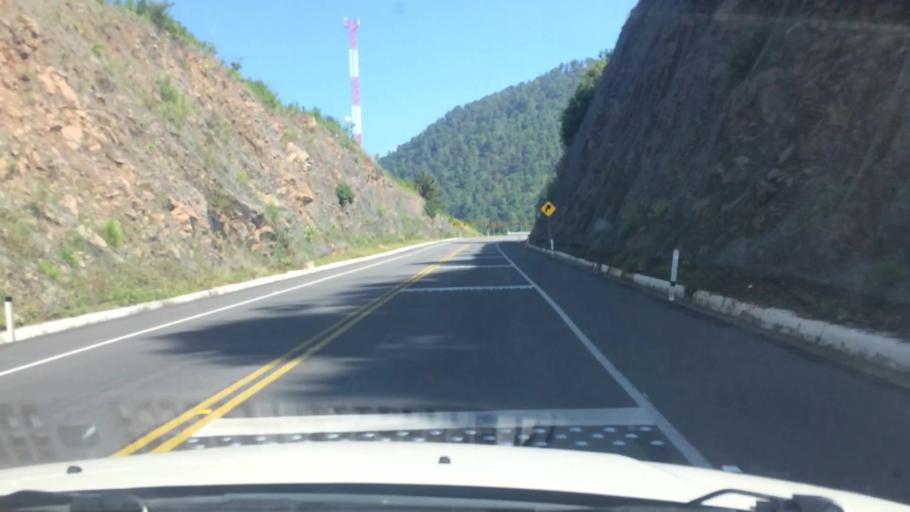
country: MX
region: Mexico
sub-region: Amanalco
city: Polvillos (San Bartolo Quinta Seccion)
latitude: 19.2310
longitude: -100.0732
